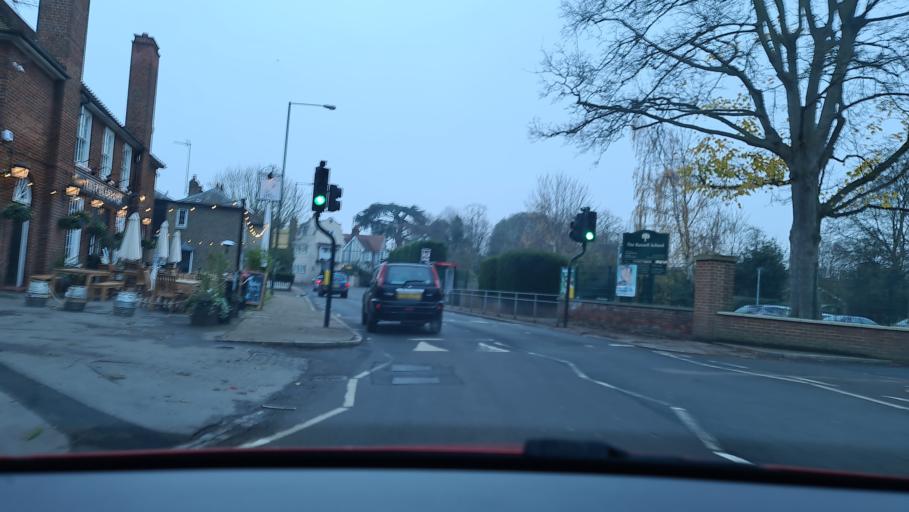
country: GB
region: England
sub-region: Greater London
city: Richmond
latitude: 51.4451
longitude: -0.3030
